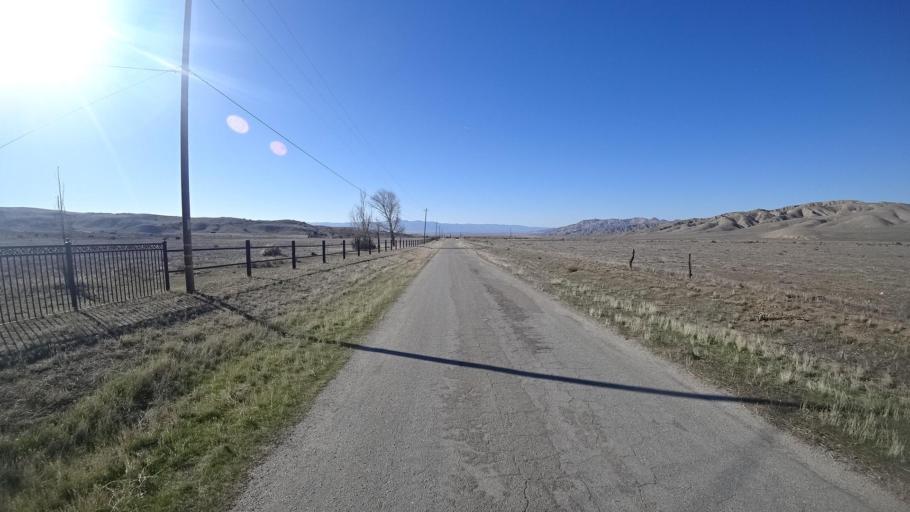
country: US
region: California
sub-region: Kern County
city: Maricopa
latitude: 34.9386
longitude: -119.4670
